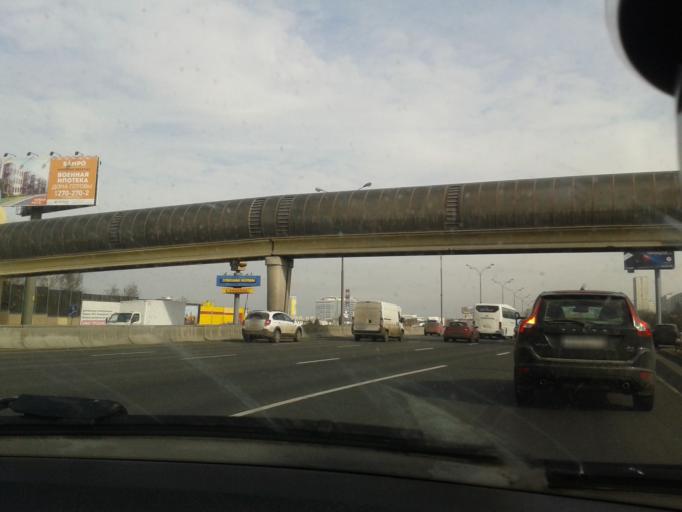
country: RU
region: Moscow
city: Strogino
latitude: 55.8020
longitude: 37.3847
